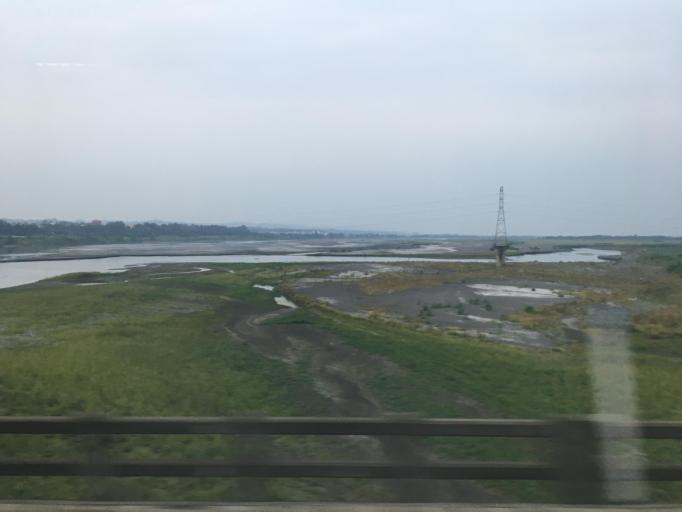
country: TW
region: Taiwan
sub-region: Pingtung
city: Pingtung
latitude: 22.6623
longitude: 120.4337
